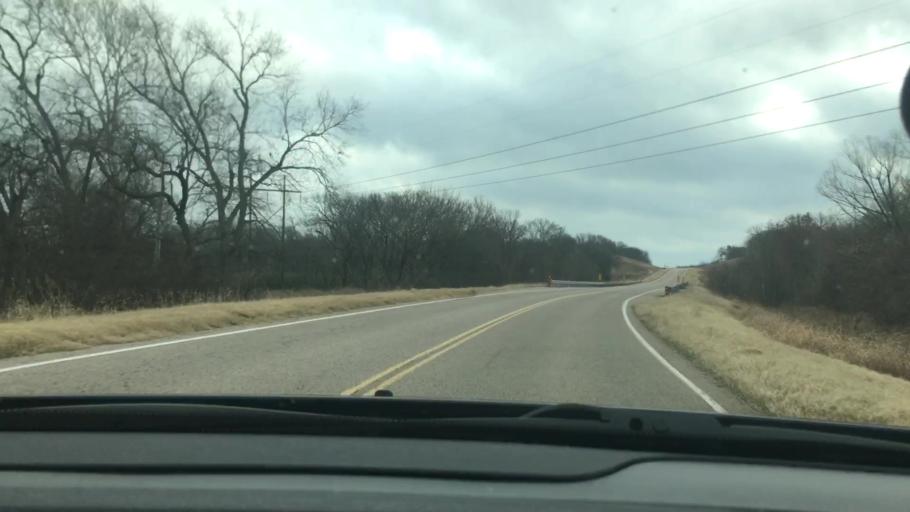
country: US
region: Oklahoma
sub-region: Bryan County
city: Durant
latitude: 34.0853
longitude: -96.3830
